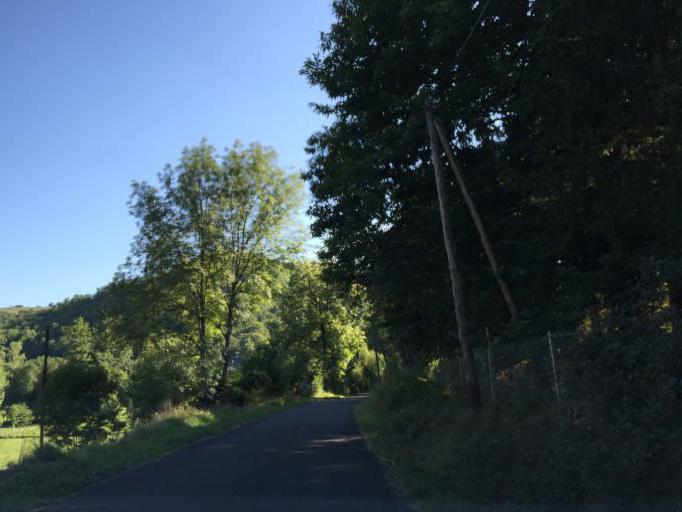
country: FR
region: Midi-Pyrenees
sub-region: Departement de l'Aveyron
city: Espalion
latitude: 44.5647
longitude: 2.6809
